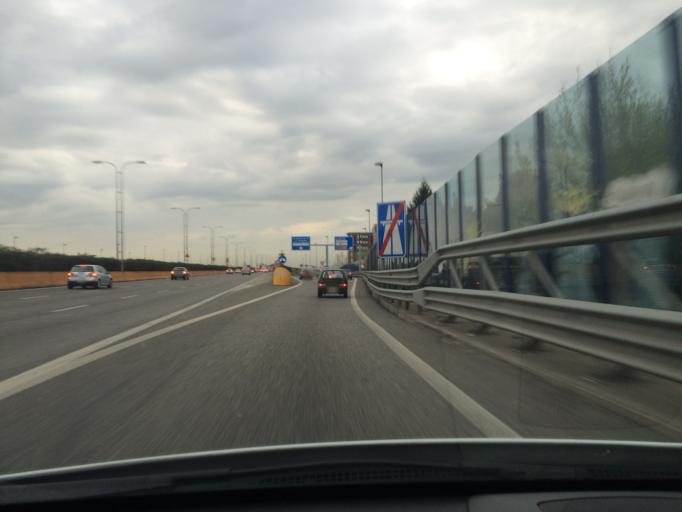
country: IT
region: Lombardy
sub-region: Provincia di Brescia
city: Roncadelle
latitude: 45.5240
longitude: 10.1800
